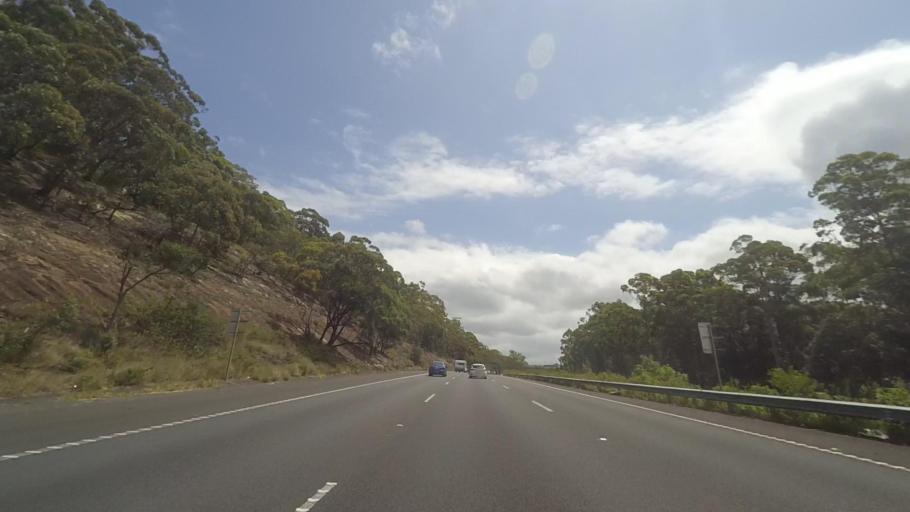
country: AU
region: New South Wales
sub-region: Gosford Shire
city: Lisarow
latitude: -33.3580
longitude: 151.3438
